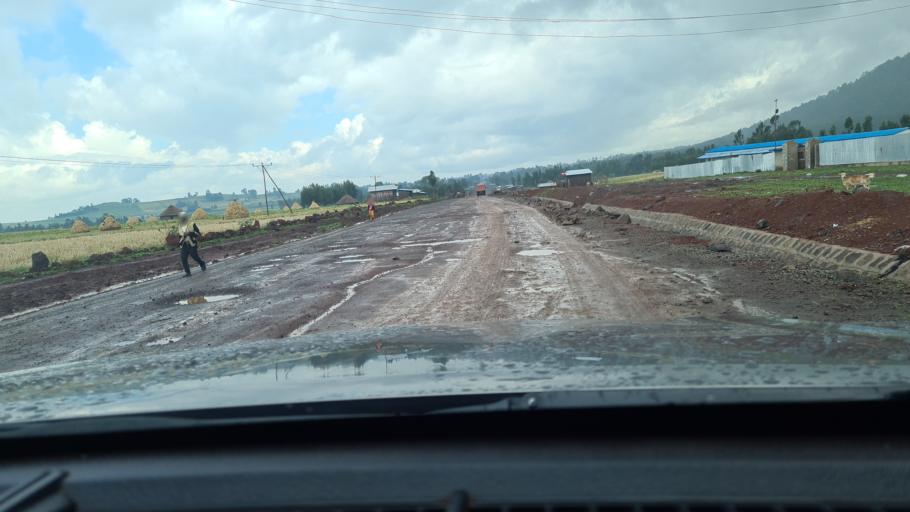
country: ET
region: Oromiya
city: Huruta
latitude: 8.0811
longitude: 39.5442
